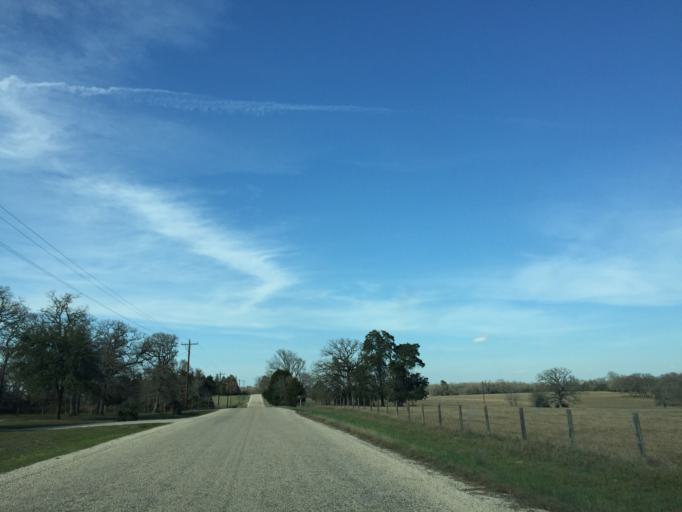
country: US
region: Texas
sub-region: Milam County
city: Thorndale
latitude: 30.4531
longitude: -97.1931
